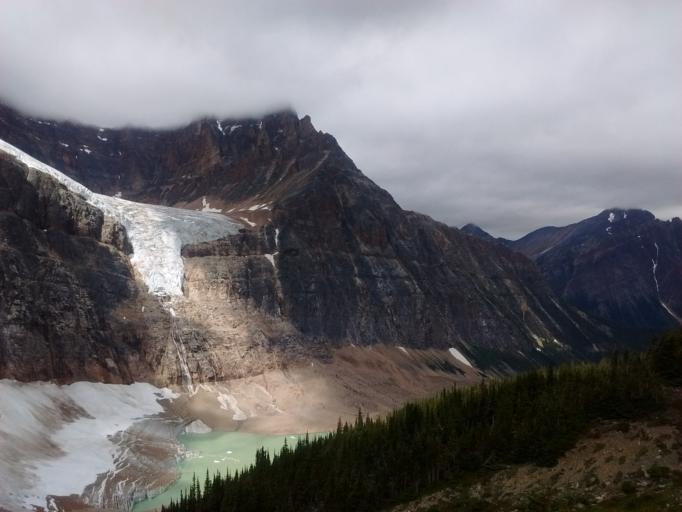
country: CA
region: Alberta
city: Jasper Park Lodge
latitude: 52.6762
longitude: -118.0331
